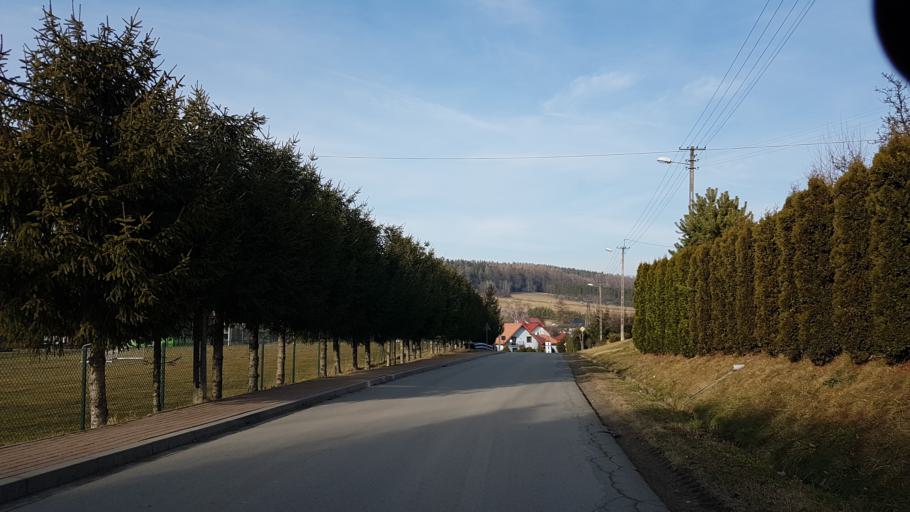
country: PL
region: Lesser Poland Voivodeship
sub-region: Powiat nowosadecki
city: Stary Sacz
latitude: 49.5461
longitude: 20.6253
